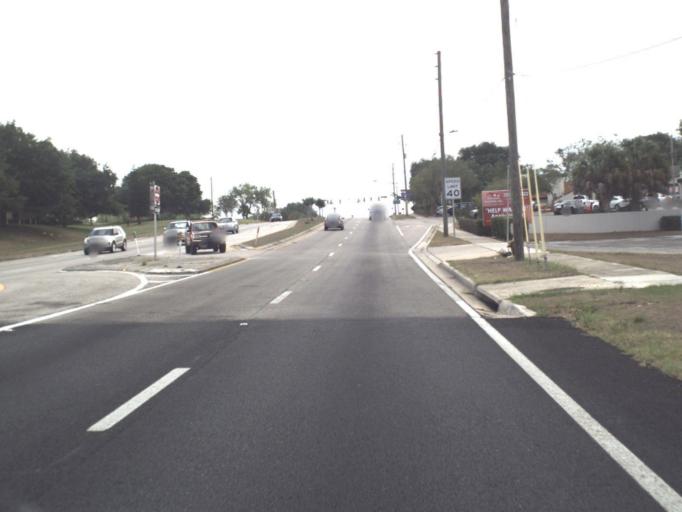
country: US
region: Florida
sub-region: Lake County
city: Clermont
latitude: 28.5538
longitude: -81.7782
